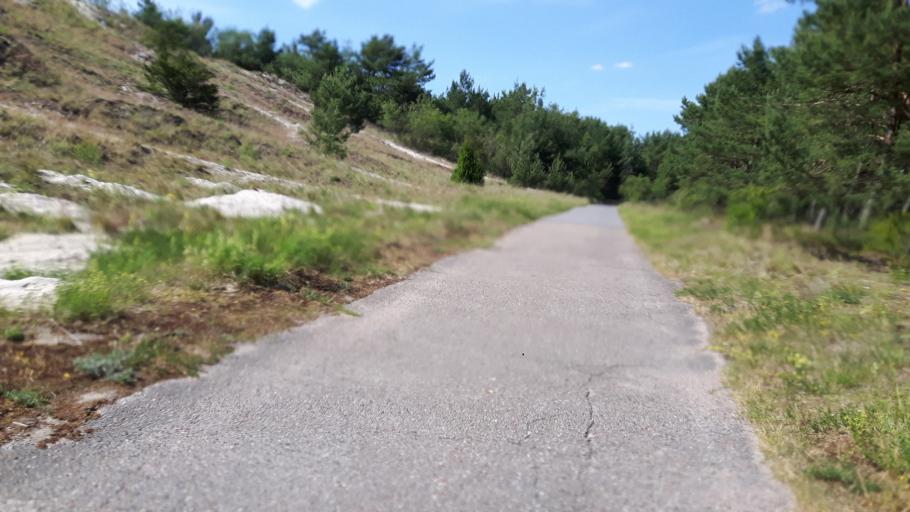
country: LT
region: Klaipedos apskritis
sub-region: Klaipeda
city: Klaipeda
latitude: 55.6957
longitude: 21.1019
